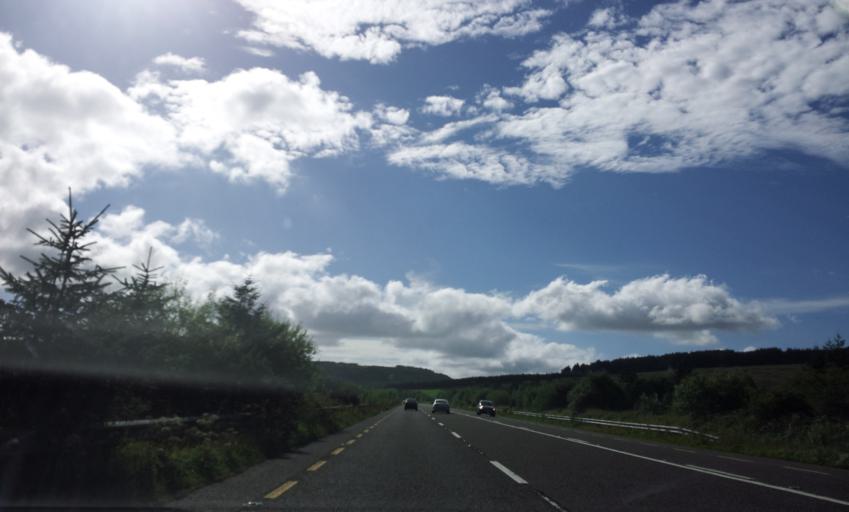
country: IE
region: Munster
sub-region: County Cork
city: Millstreet
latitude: 51.9619
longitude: -9.2216
